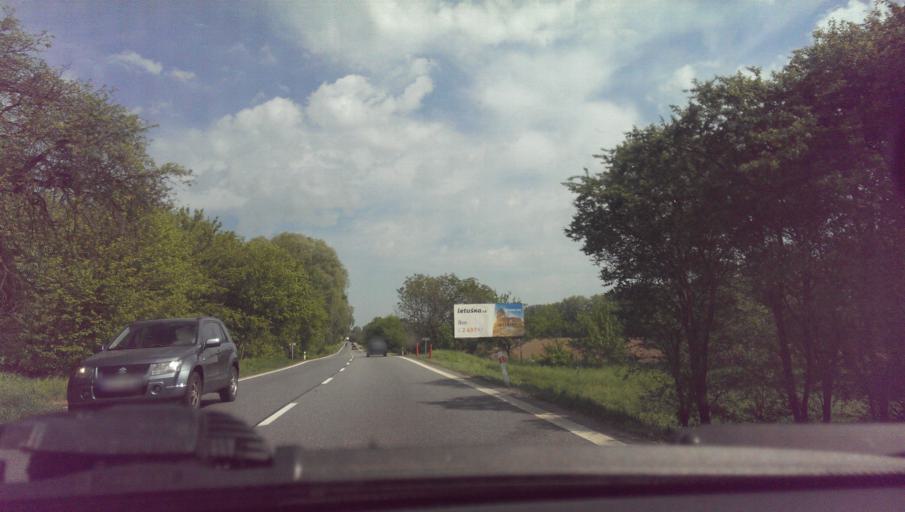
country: CZ
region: Zlin
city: Spytihnev
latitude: 49.1530
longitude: 17.5035
